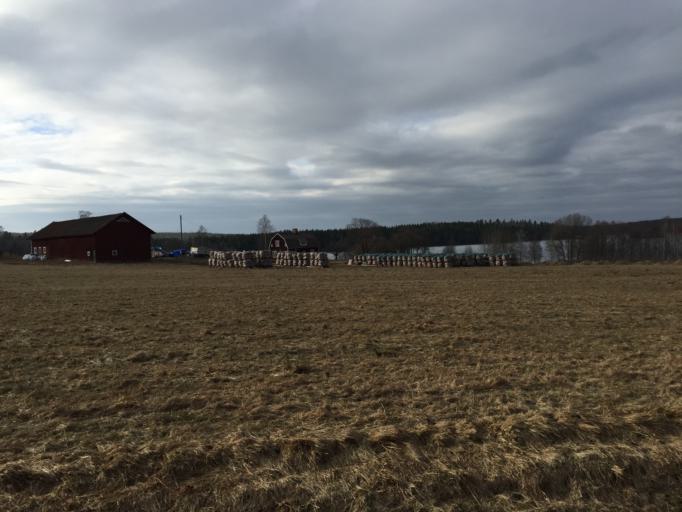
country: SE
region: Soedermanland
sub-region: Vingakers Kommun
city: Vingaker
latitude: 58.9979
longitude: 15.6757
